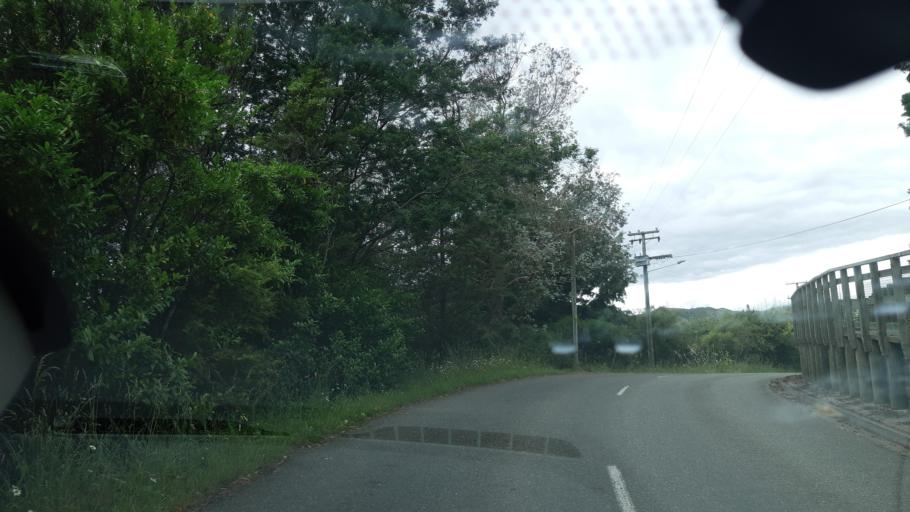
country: NZ
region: Tasman
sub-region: Tasman District
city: Wakefield
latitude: -41.4097
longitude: 173.0477
